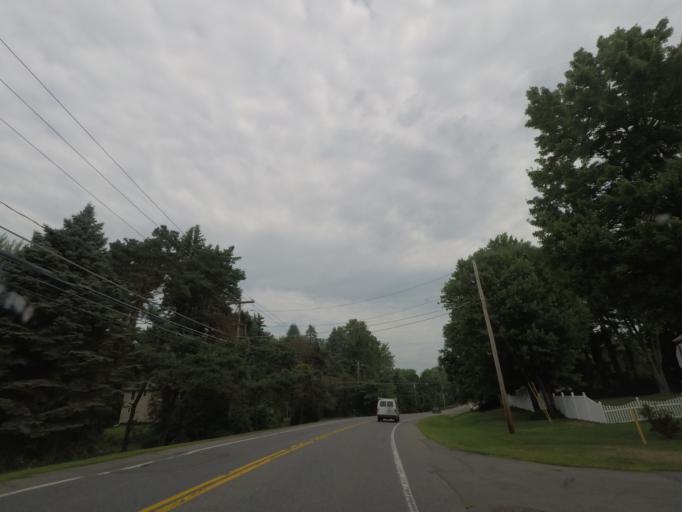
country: US
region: New York
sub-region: Saratoga County
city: Waterford
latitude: 42.8057
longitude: -73.6844
